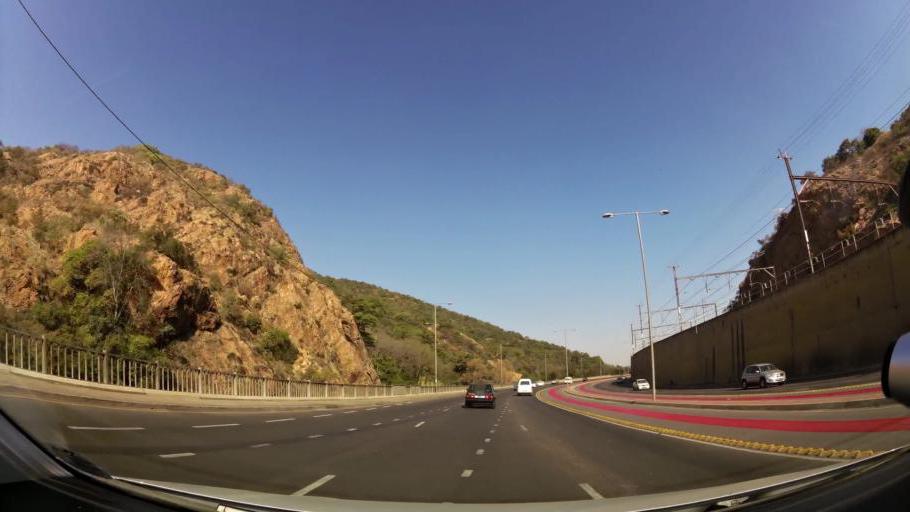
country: ZA
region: Gauteng
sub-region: City of Tshwane Metropolitan Municipality
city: Pretoria
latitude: -25.6891
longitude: 28.1873
